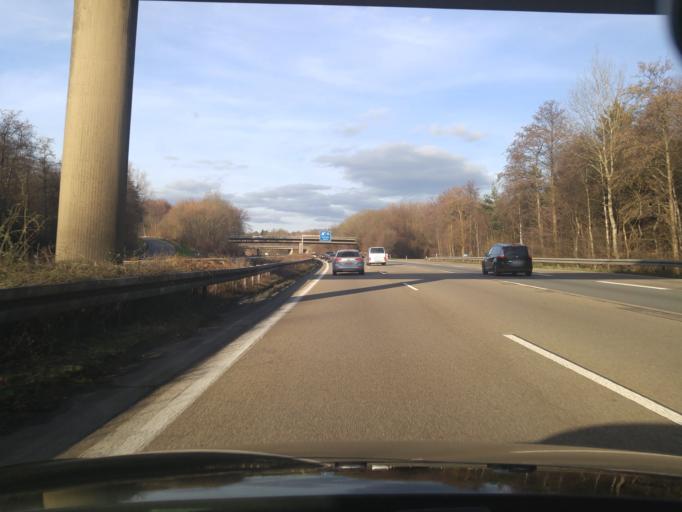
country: DE
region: North Rhine-Westphalia
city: Leichlingen
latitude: 51.1091
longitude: 6.9879
